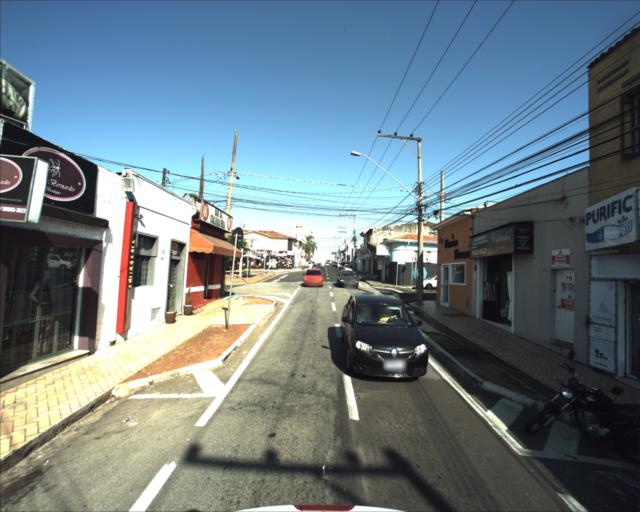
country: BR
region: Sao Paulo
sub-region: Sorocaba
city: Sorocaba
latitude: -23.4930
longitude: -47.4558
